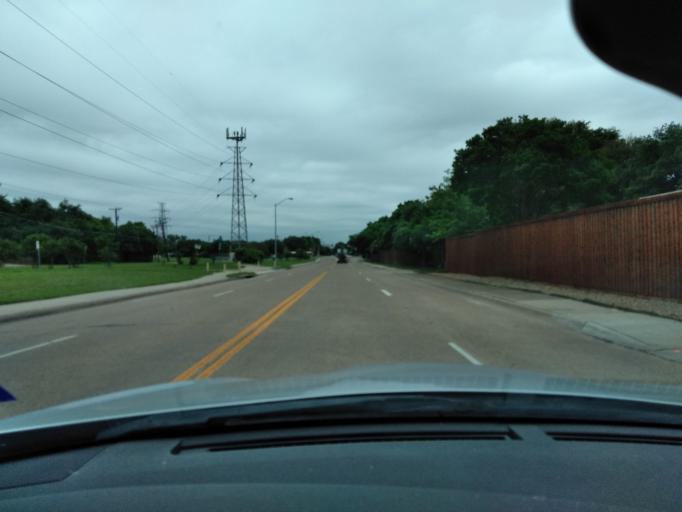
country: US
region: Texas
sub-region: Dallas County
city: Richardson
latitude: 32.9529
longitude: -96.7787
